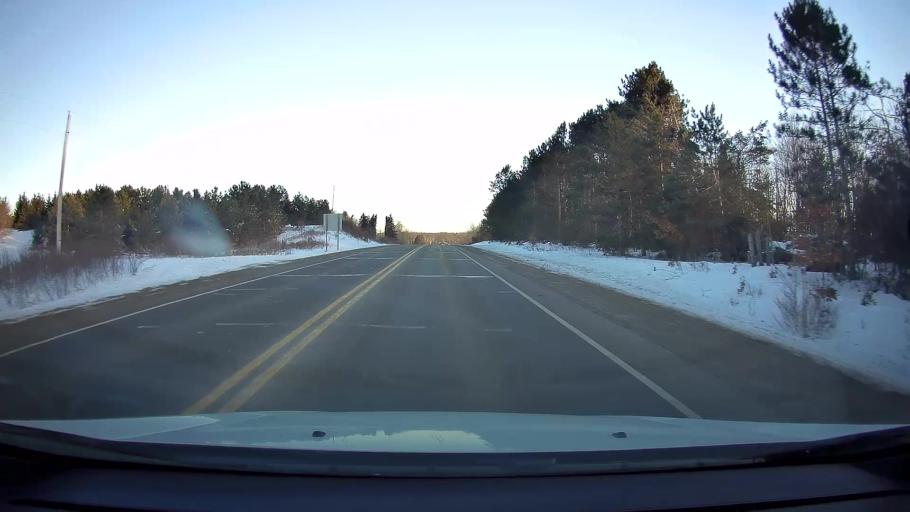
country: US
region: Wisconsin
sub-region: Barron County
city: Turtle Lake
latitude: 45.4043
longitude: -92.1400
